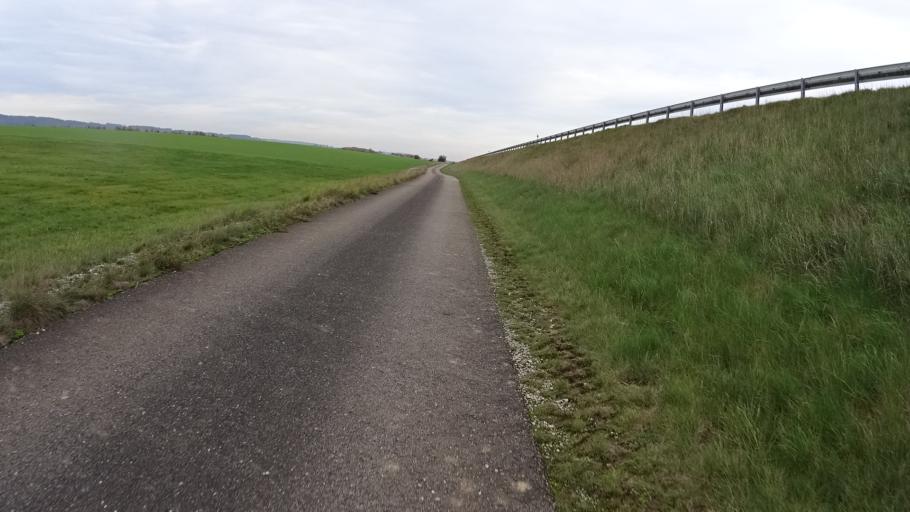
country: DE
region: Bavaria
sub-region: Upper Bavaria
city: Eitensheim
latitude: 48.8260
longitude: 11.3355
